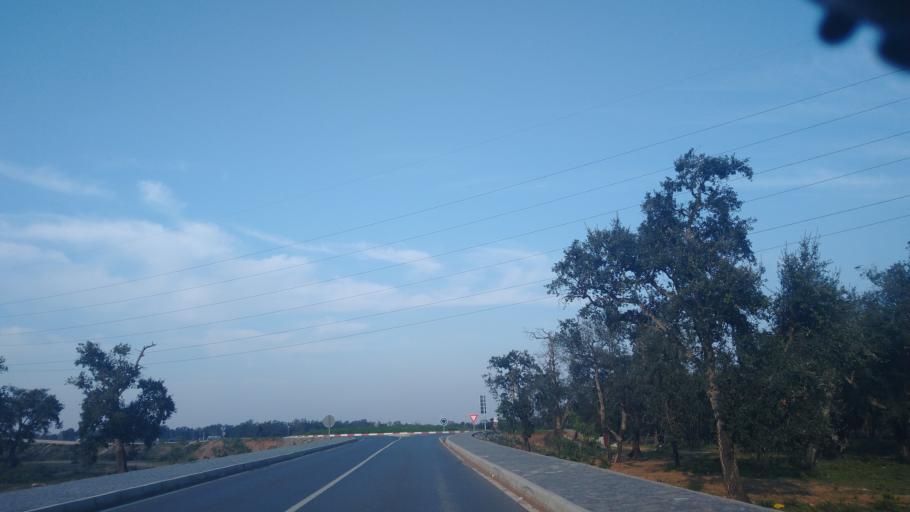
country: MA
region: Rabat-Sale-Zemmour-Zaer
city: Sale
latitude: 33.9969
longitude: -6.7186
